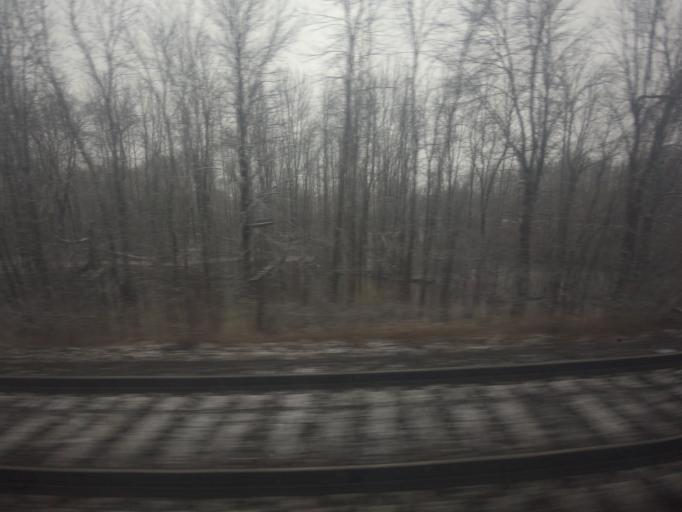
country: CA
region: Ontario
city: Brockville
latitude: 44.5661
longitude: -75.7747
